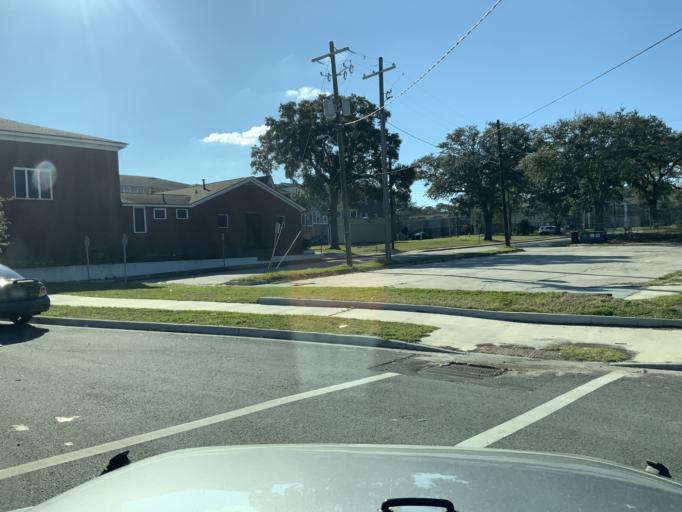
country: US
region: Georgia
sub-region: Chatham County
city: Savannah
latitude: 32.0738
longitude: -81.0822
